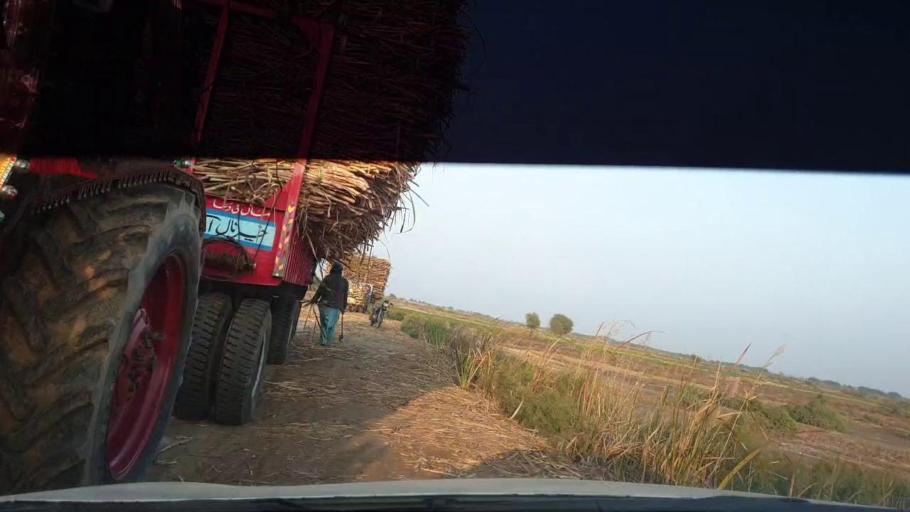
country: PK
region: Sindh
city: Berani
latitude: 25.7456
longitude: 68.9728
